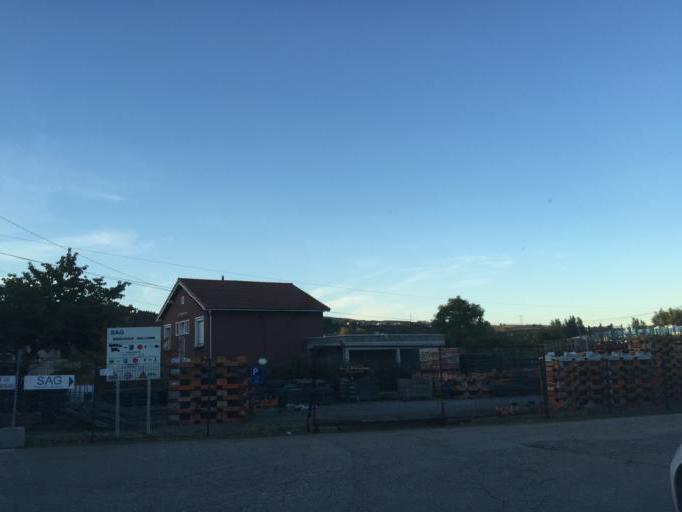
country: FR
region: Rhone-Alpes
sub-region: Departement de la Loire
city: La Grand-Croix
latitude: 45.4931
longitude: 4.5559
